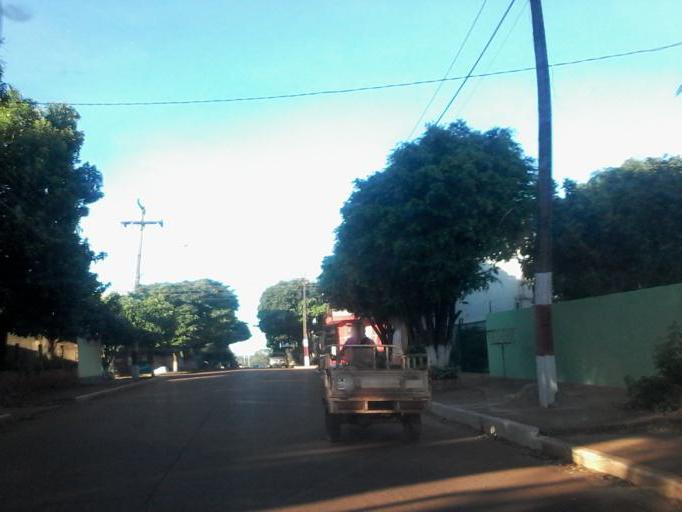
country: PY
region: Alto Parana
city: Ciudad del Este
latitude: -25.4366
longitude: -54.6419
